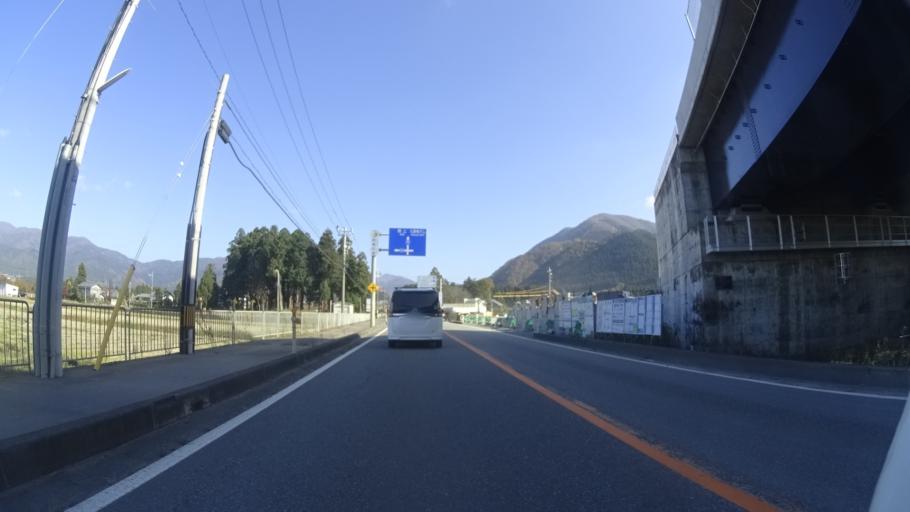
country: JP
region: Fukui
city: Ono
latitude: 35.9738
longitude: 136.5545
